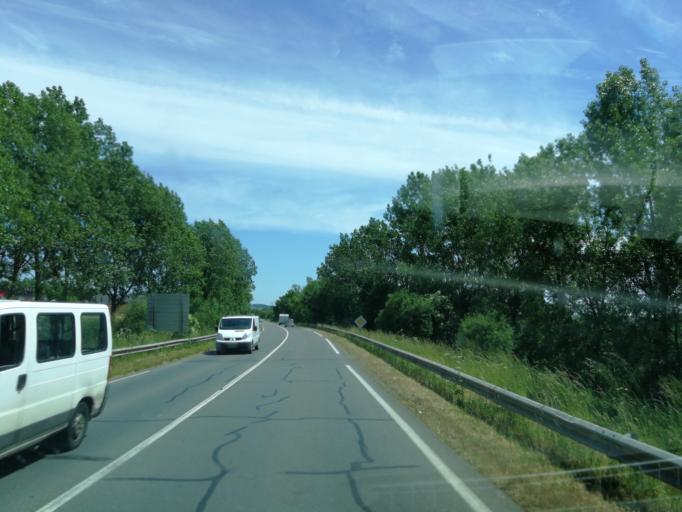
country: FR
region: Pays de la Loire
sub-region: Departement de la Vendee
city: La Chataigneraie
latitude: 46.6402
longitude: -0.7505
